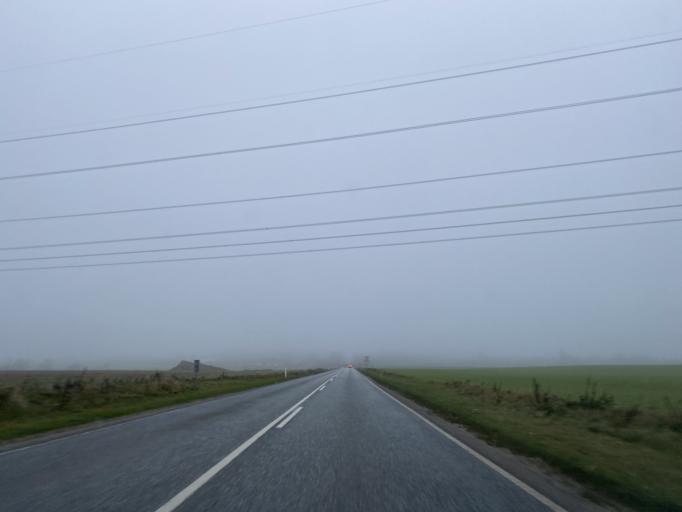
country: DK
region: Central Jutland
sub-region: Arhus Kommune
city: Solbjerg
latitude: 55.9742
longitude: 10.0579
